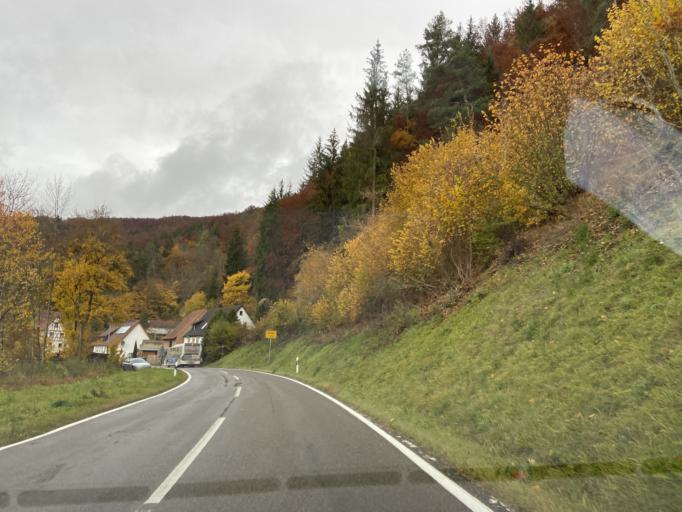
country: DE
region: Baden-Wuerttemberg
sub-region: Tuebingen Region
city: Stetten am Kalten Markt
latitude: 48.0949
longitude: 9.0679
